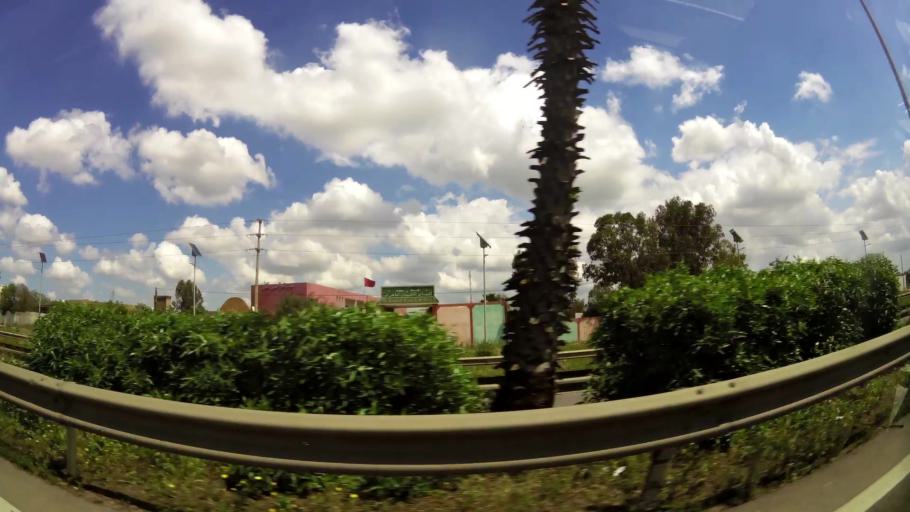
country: MA
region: Chaouia-Ouardigha
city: Nouaseur
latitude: 33.4179
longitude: -7.6268
